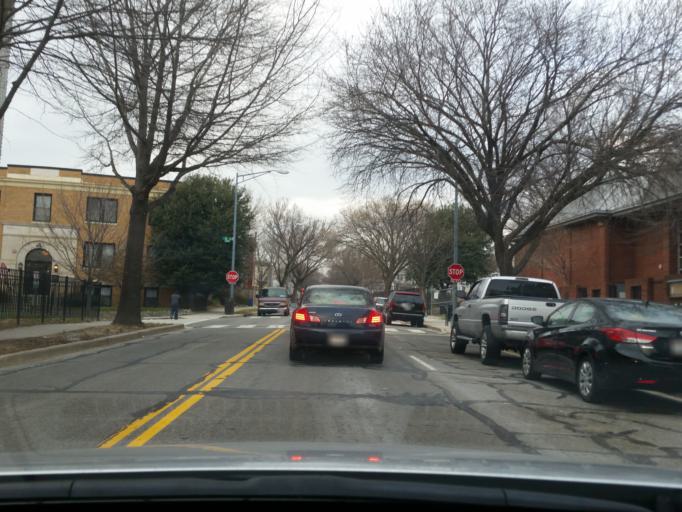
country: US
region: Washington, D.C.
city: Washington, D.C.
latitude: 38.9138
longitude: -77.0083
